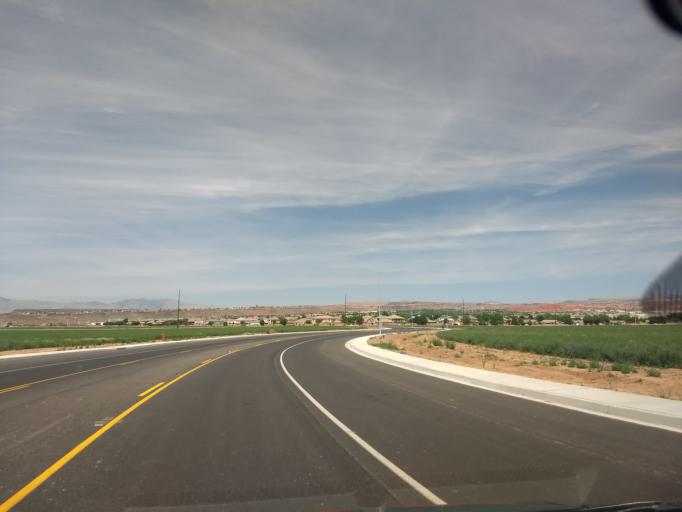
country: US
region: Utah
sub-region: Washington County
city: Washington
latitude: 37.0945
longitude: -113.5054
